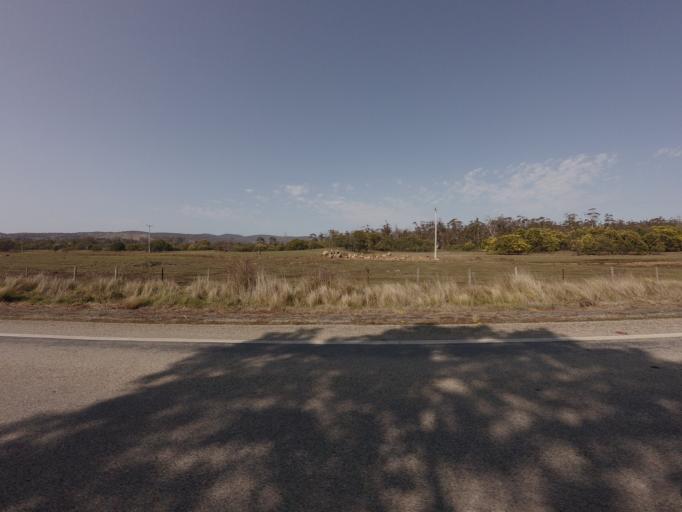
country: AU
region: Tasmania
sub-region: Northern Midlands
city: Evandale
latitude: -41.8291
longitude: 147.4935
